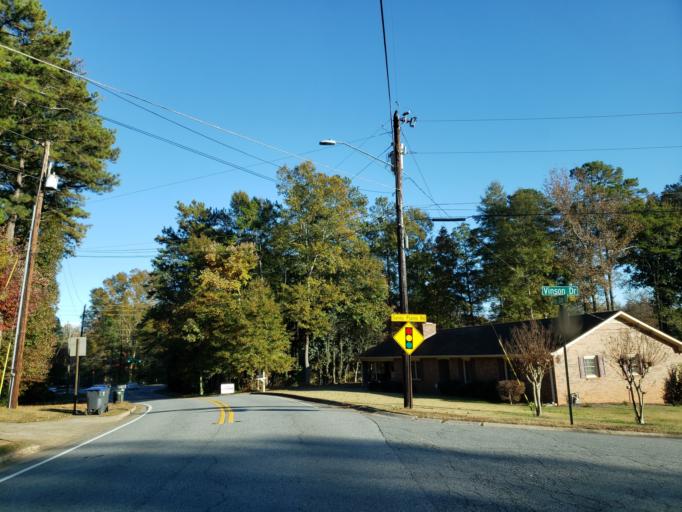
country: US
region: Georgia
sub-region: Cherokee County
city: Woodstock
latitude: 34.0468
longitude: -84.4573
